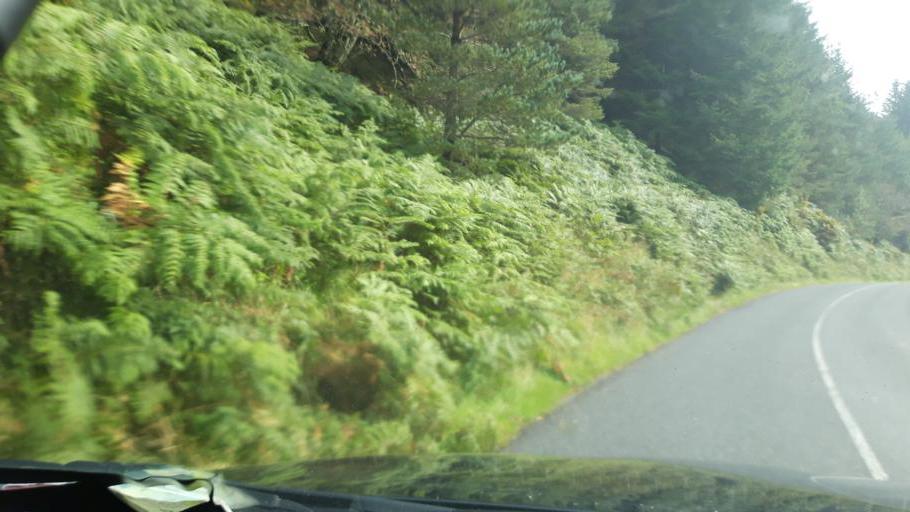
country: IE
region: Leinster
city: Ballinteer
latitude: 53.2330
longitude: -6.2764
